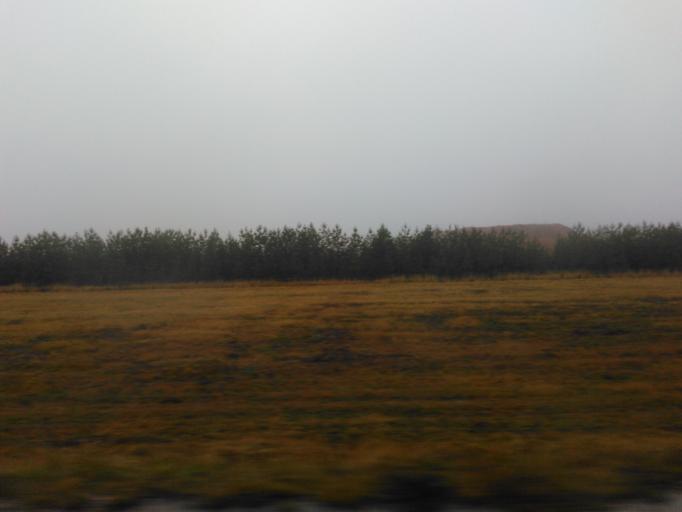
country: RU
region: Tatarstan
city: Sviyazhsk
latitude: 55.7373
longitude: 48.7834
